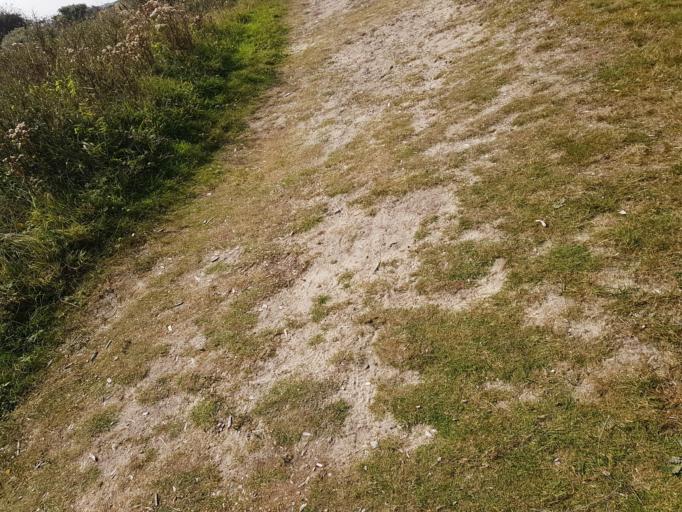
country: NL
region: North Holland
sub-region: Gemeente Texel
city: Den Burg
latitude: 53.1789
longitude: 4.8514
